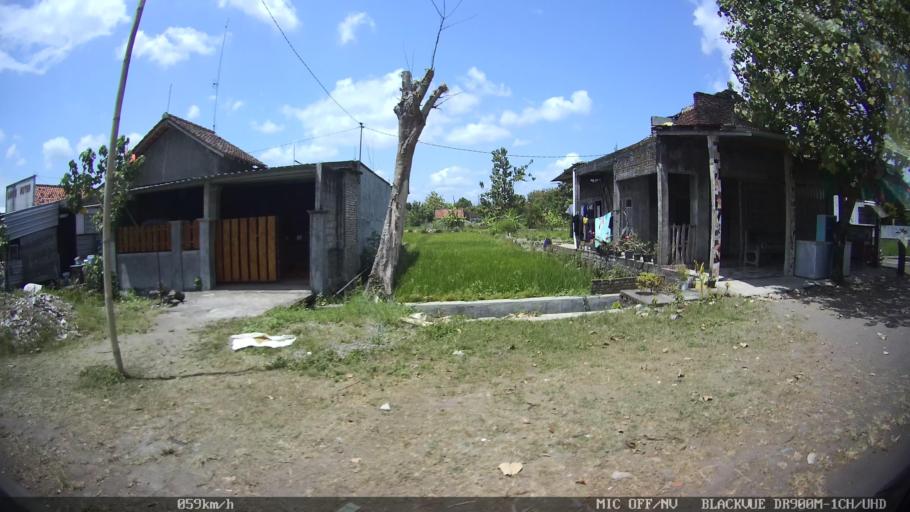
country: ID
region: Daerah Istimewa Yogyakarta
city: Bantul
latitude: -7.8934
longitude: 110.3470
